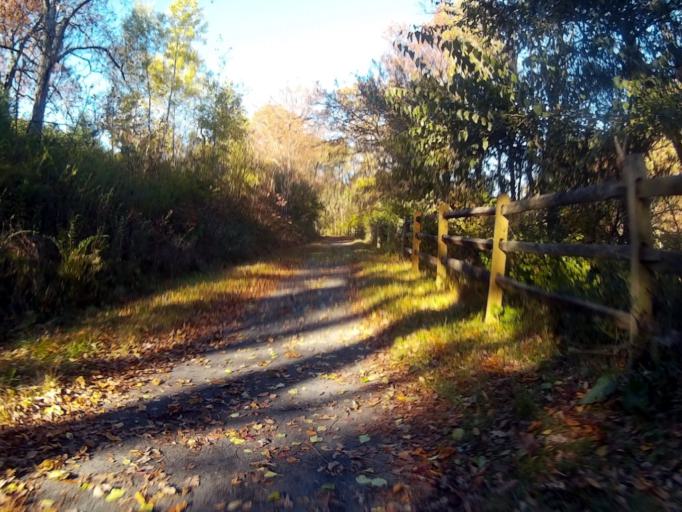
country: US
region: Pennsylvania
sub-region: Centre County
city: State College
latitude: 40.8148
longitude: -77.8766
